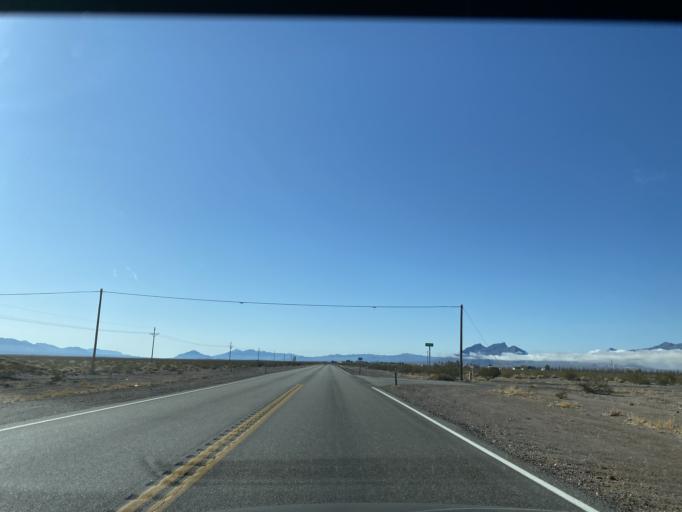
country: US
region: Nevada
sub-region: Nye County
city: Beatty
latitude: 36.5117
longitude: -116.4205
